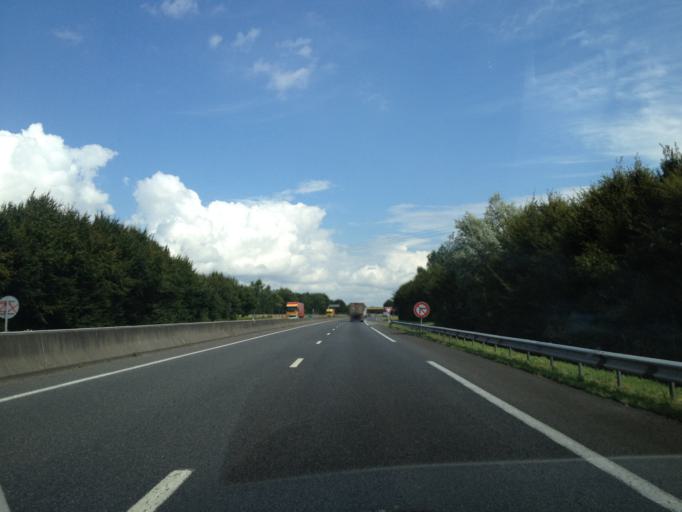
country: FR
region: Picardie
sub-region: Departement de la Somme
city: Oisemont
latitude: 50.0440
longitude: 1.7605
